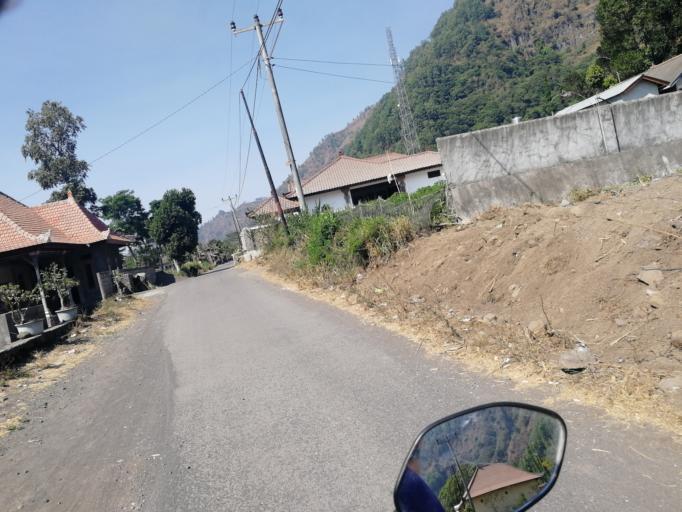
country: ID
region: Bali
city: Banjar Buahan
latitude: -8.2762
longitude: 115.4131
